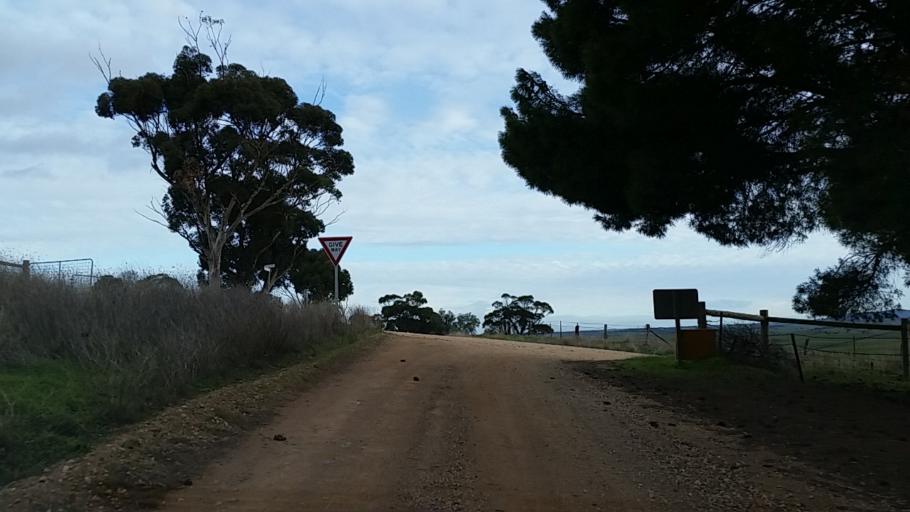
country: AU
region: South Australia
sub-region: Mount Barker
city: Callington
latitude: -35.0009
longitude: 139.0497
